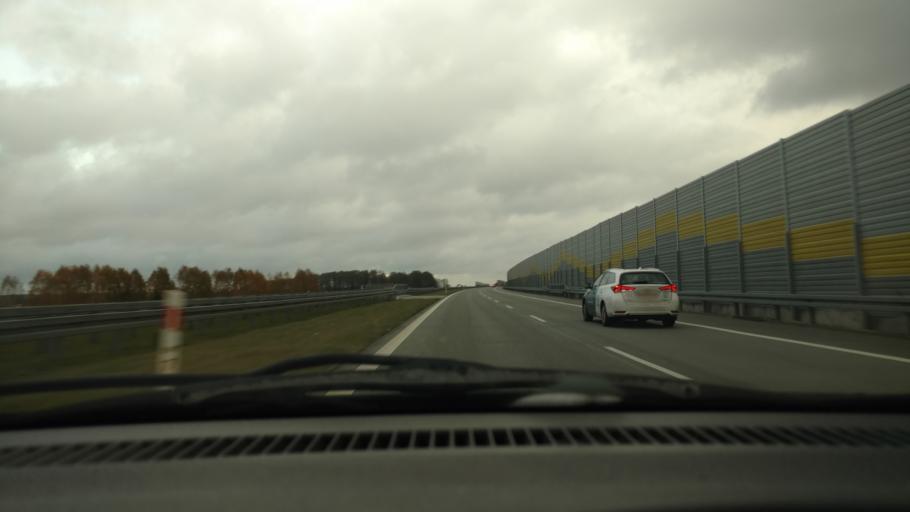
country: PL
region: Lodz Voivodeship
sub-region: Powiat pabianicki
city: Pabianice
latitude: 51.6241
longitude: 19.3893
